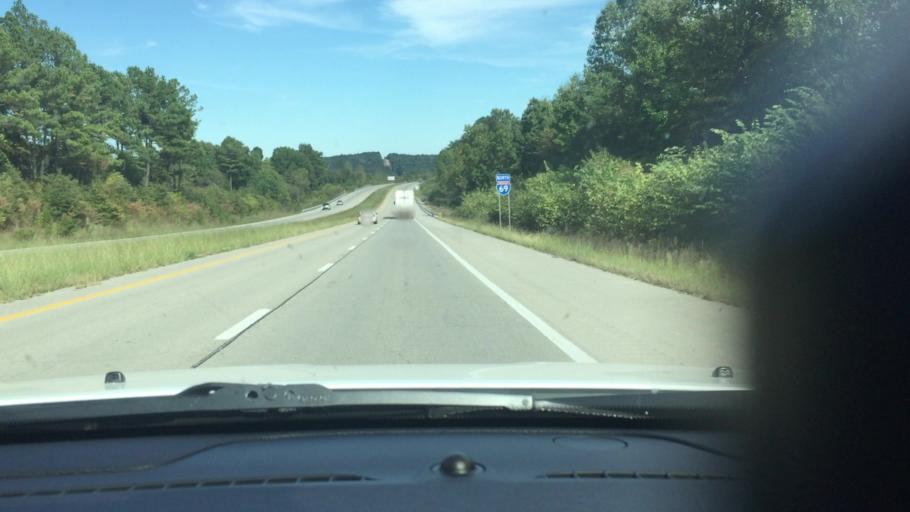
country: US
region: Kentucky
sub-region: Caldwell County
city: Princeton
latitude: 37.1356
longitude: -87.8623
